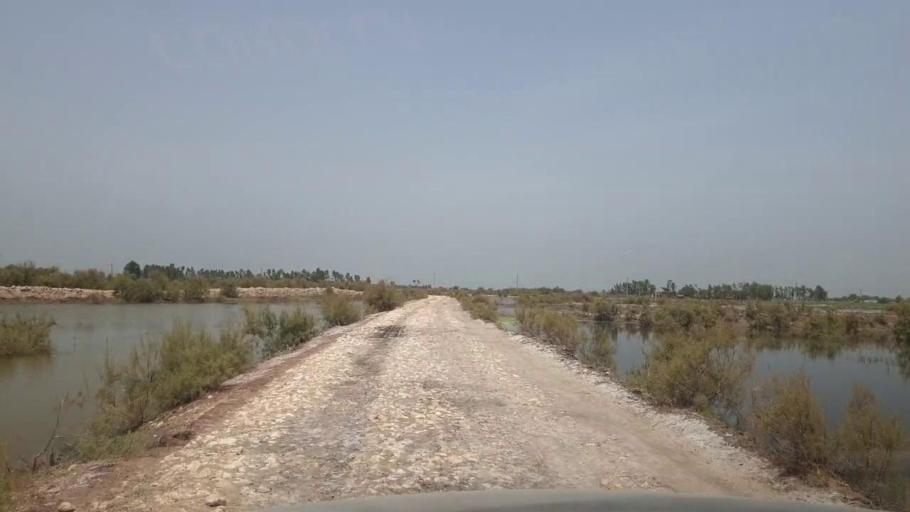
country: PK
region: Sindh
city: Garhi Yasin
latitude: 27.9172
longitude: 68.4149
